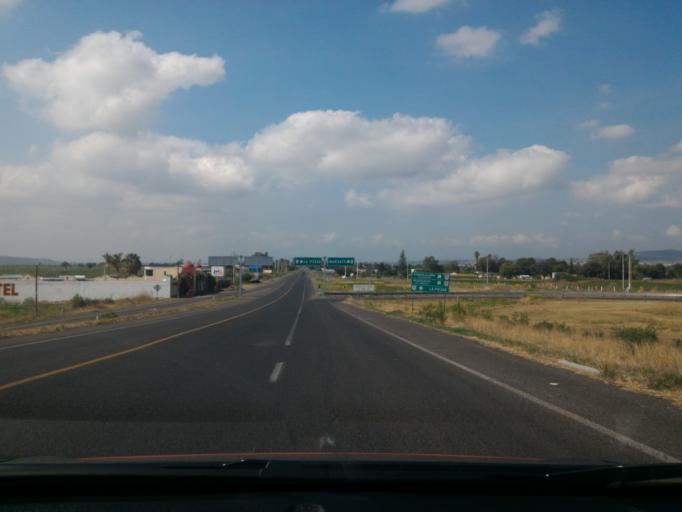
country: MX
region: Guanajuato
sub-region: Penjamo
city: Estacion la Piedad
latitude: 20.3938
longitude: -102.0000
